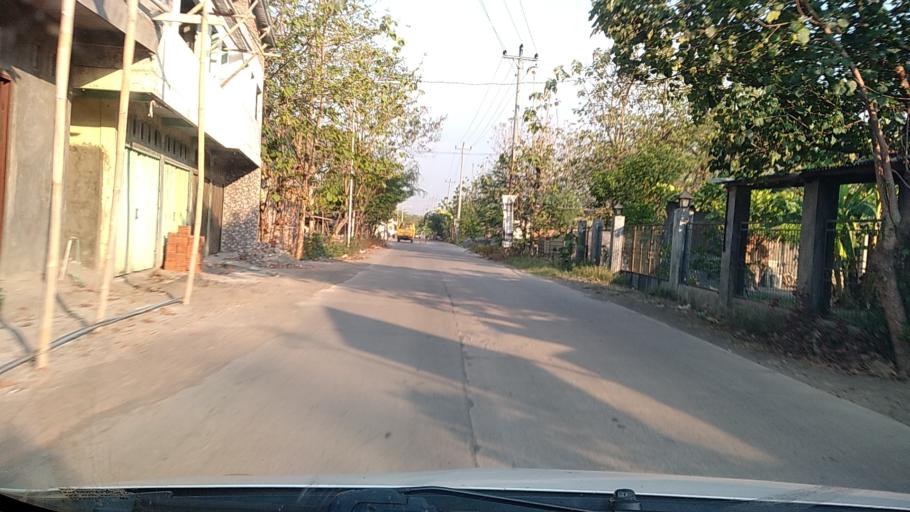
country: ID
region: Central Java
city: Mranggen
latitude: -7.0655
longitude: 110.4718
